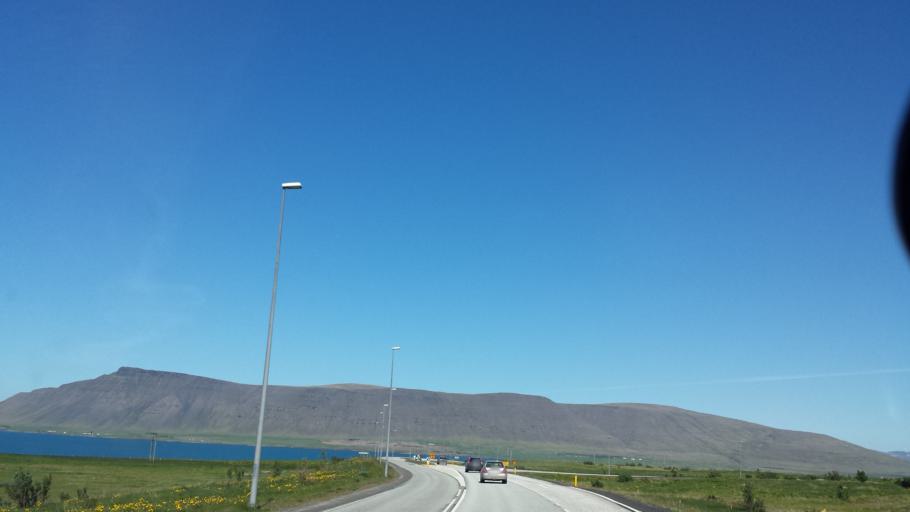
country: IS
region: Capital Region
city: Reykjavik
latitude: 64.2726
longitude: -21.8363
